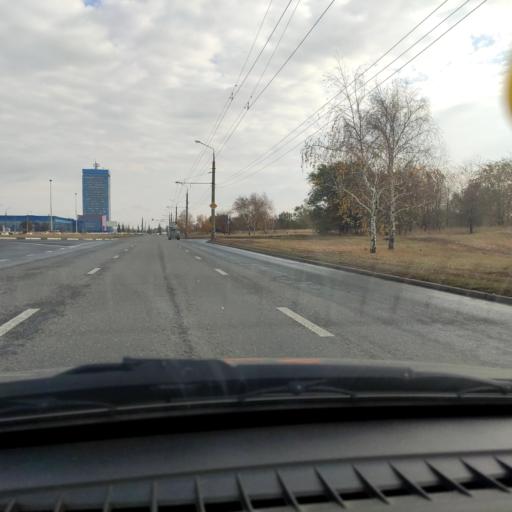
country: RU
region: Samara
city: Tol'yatti
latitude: 53.5561
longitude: 49.2521
